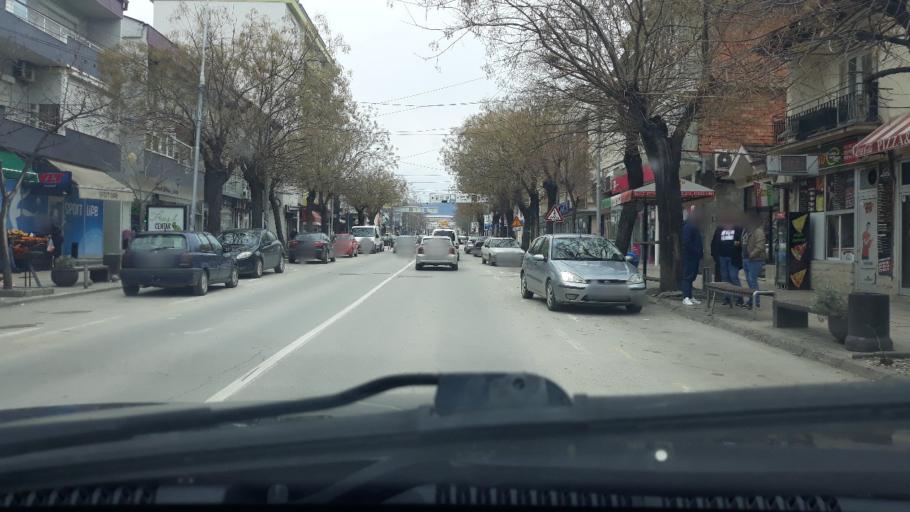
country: MK
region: Kavadarci
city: Kavadarci
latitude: 41.4359
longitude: 22.0112
